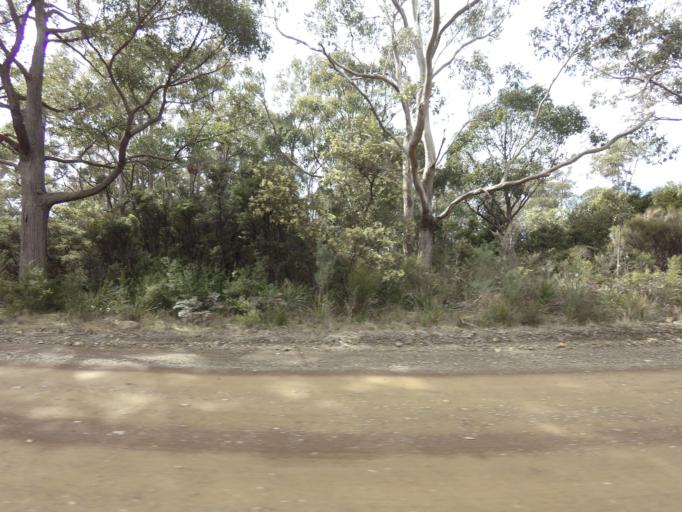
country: AU
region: Tasmania
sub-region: Huon Valley
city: Geeveston
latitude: -43.4465
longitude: 146.9050
